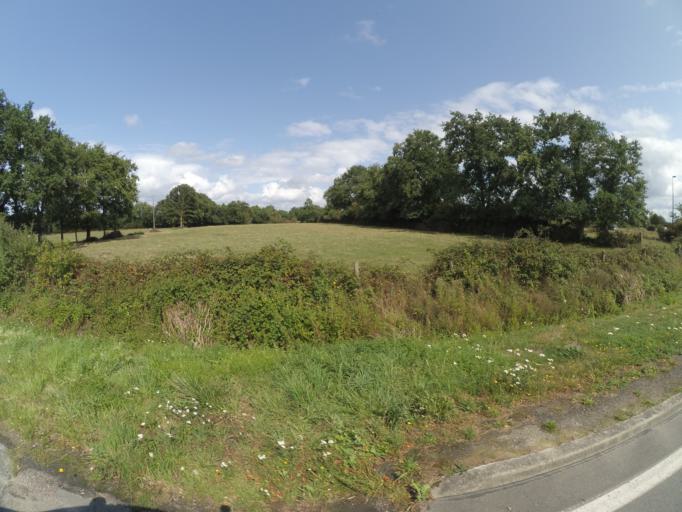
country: FR
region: Pays de la Loire
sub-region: Departement de la Vendee
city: La Bruffiere
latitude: 47.0215
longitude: -1.2015
